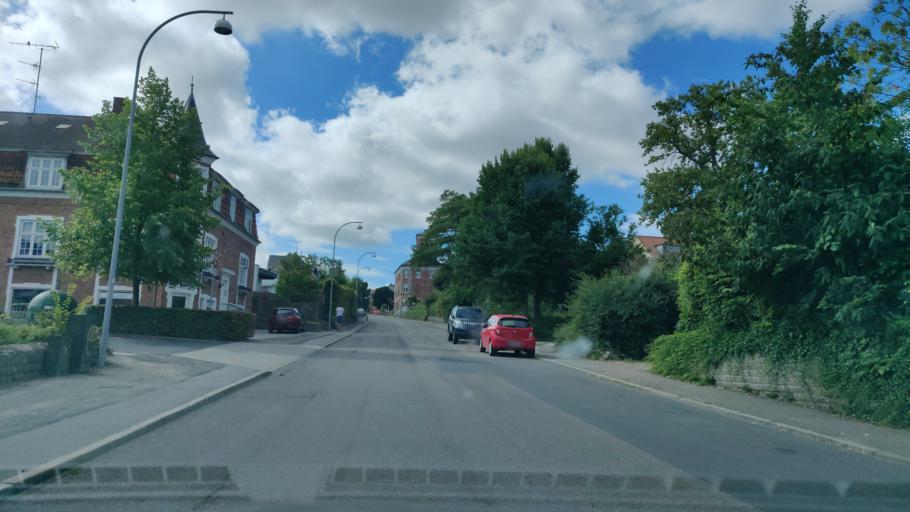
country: DK
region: Zealand
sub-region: Roskilde Kommune
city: Roskilde
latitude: 55.6464
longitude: 12.0835
